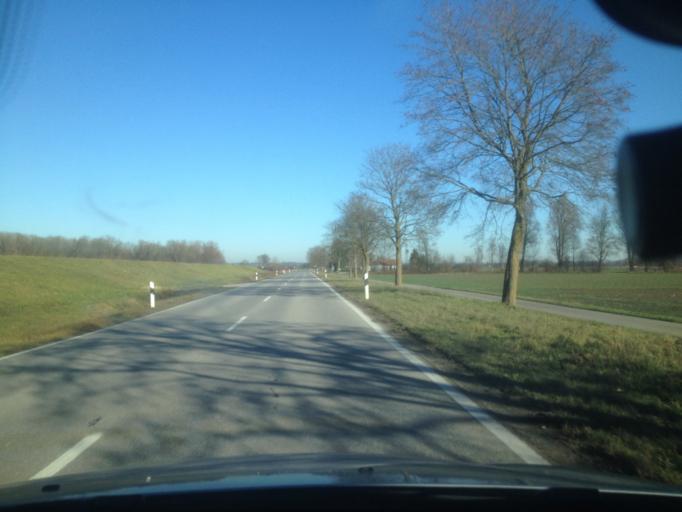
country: DE
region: Bavaria
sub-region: Upper Bavaria
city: Langenpreising
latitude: 48.4448
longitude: 11.9432
